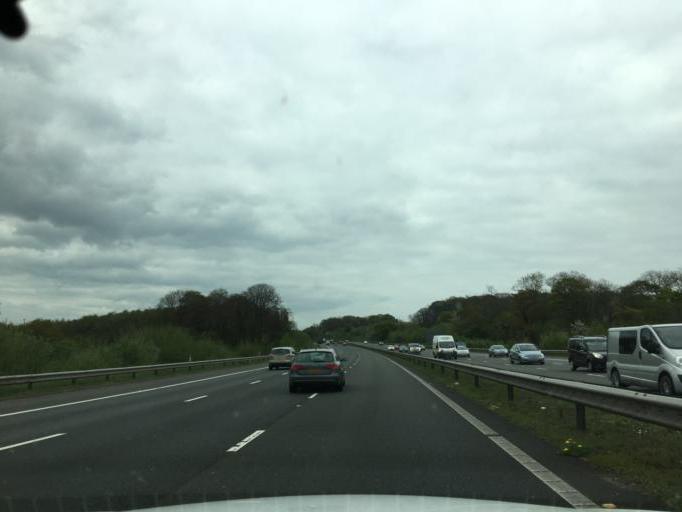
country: GB
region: Wales
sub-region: Newport
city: Marshfield
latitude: 51.5421
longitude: -3.1141
